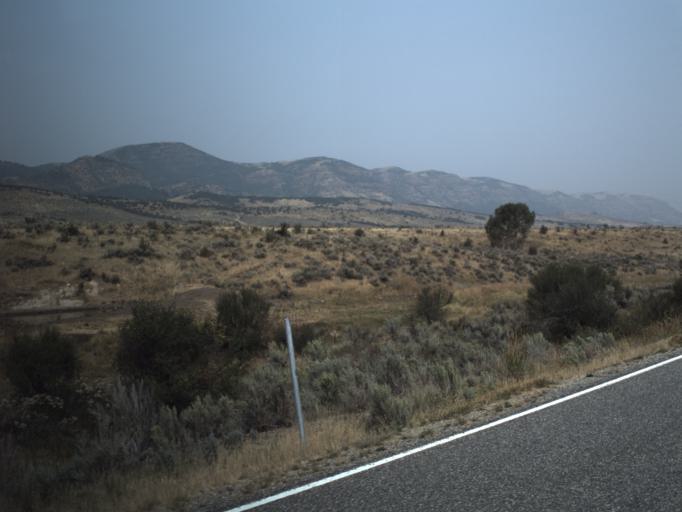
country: US
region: Utah
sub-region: Morgan County
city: Morgan
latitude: 40.9641
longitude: -111.5457
